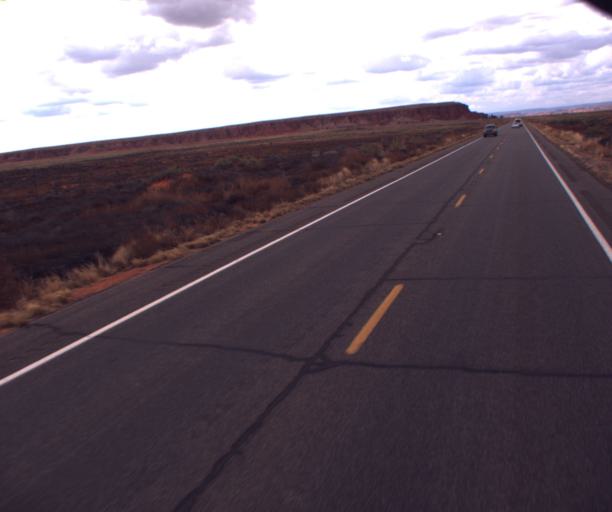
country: US
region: Arizona
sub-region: Navajo County
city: Kayenta
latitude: 36.7818
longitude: -109.9847
